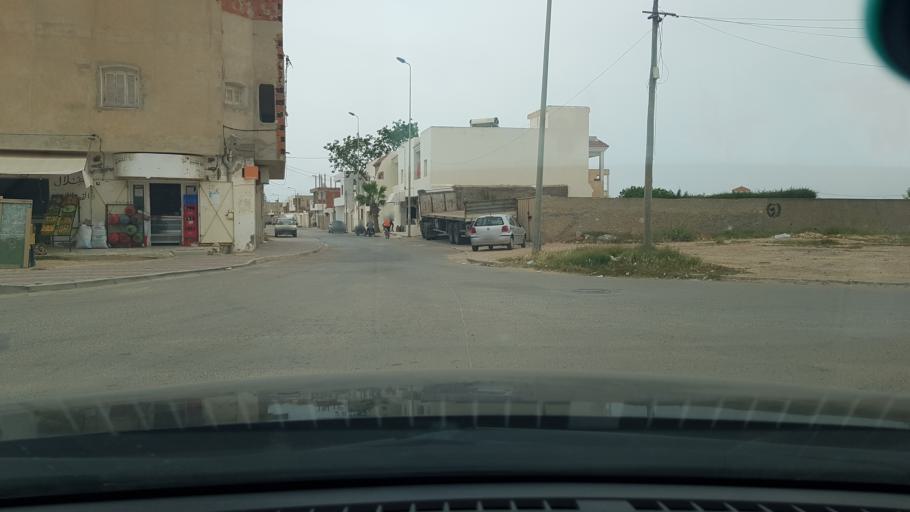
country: TN
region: Safaqis
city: Al Qarmadah
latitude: 34.8255
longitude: 10.7532
